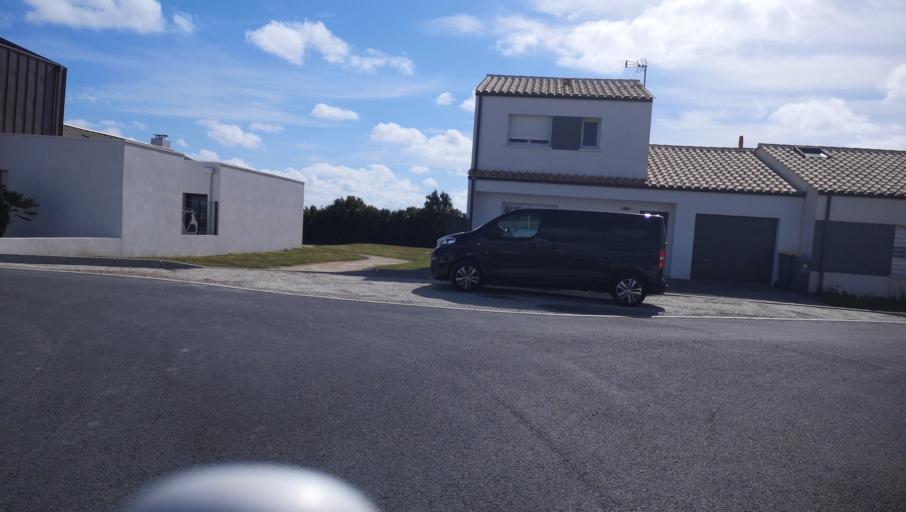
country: FR
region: Pays de la Loire
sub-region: Departement de la Vendee
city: Les Sables-d'Olonne
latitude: 46.5108
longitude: -1.7903
